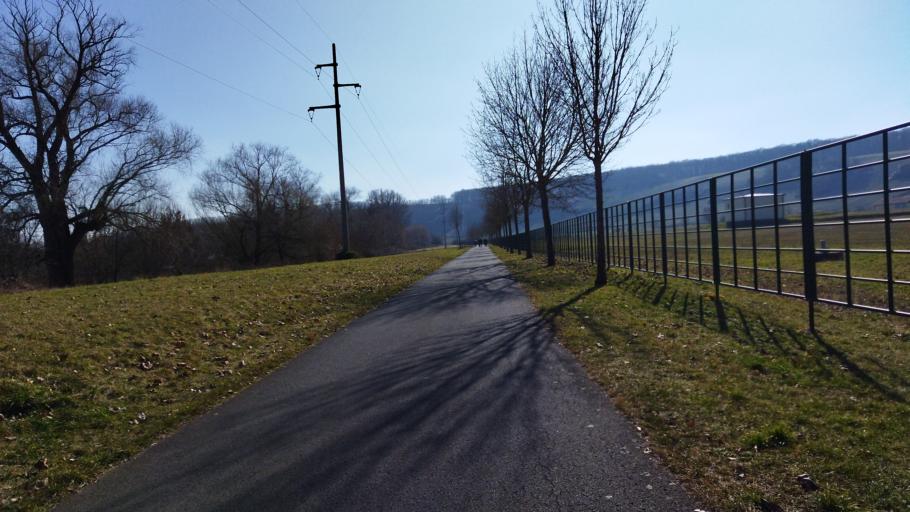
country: DE
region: Bavaria
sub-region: Regierungsbezirk Unterfranken
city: Marktsteft
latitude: 49.6969
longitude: 10.1296
